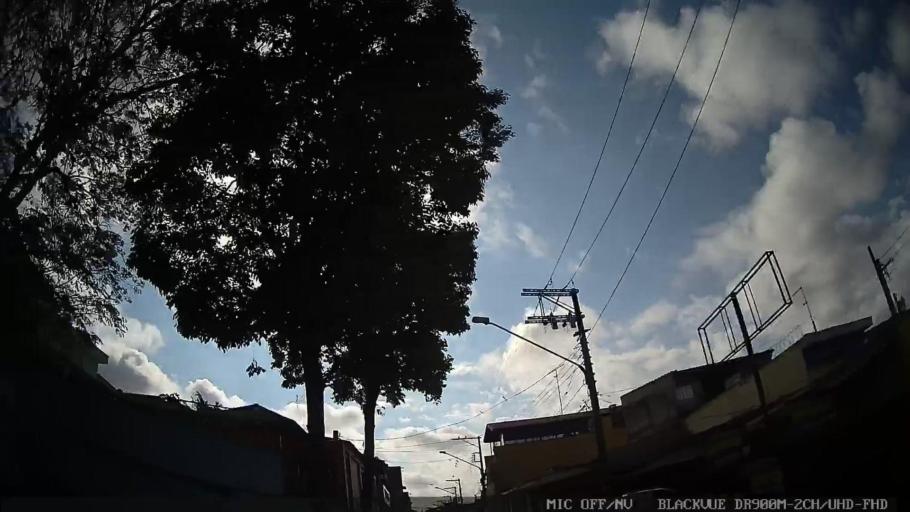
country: BR
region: Sao Paulo
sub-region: Sao Caetano Do Sul
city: Sao Caetano do Sul
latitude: -23.5479
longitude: -46.5019
